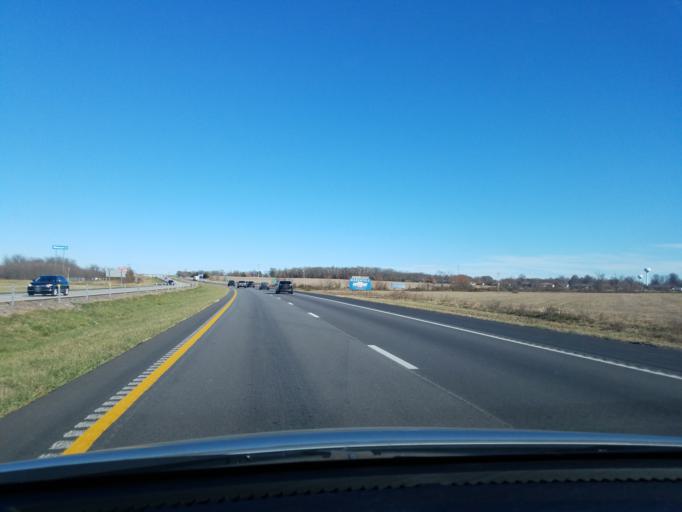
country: US
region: Missouri
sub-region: Webster County
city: Marshfield
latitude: 37.3333
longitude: -92.9416
